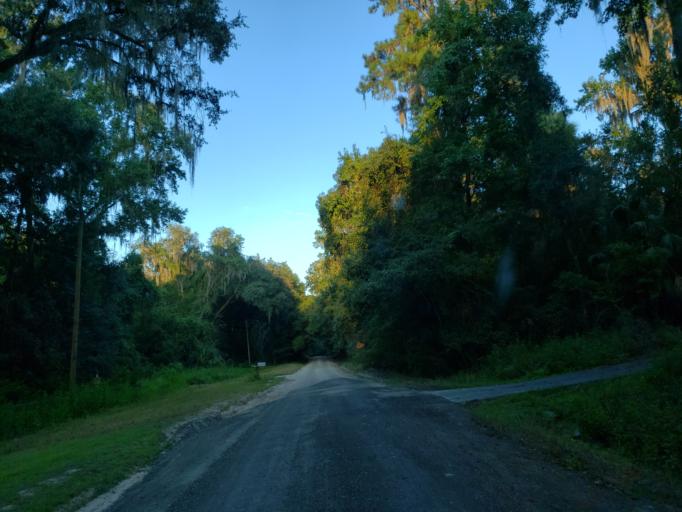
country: US
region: Florida
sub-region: Marion County
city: Citra
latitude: 29.4842
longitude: -82.2653
